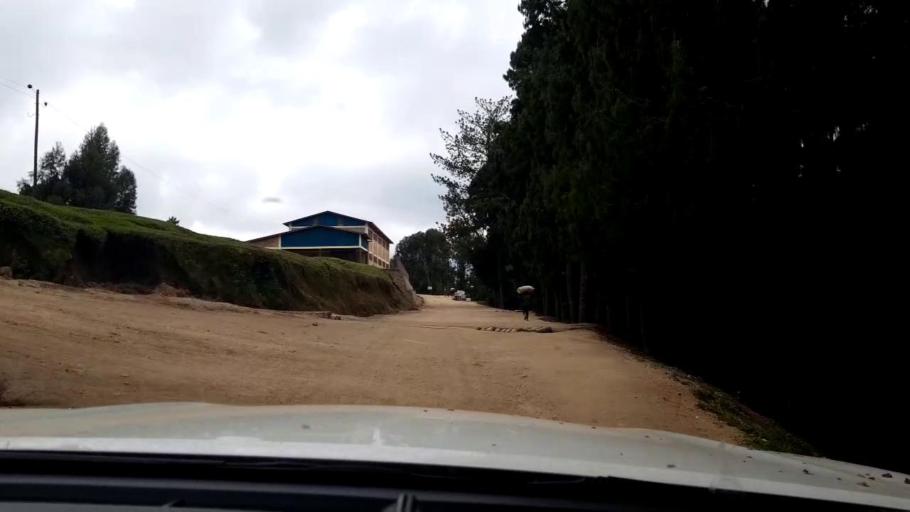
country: RW
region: Western Province
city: Kibuye
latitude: -1.8896
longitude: 29.5263
